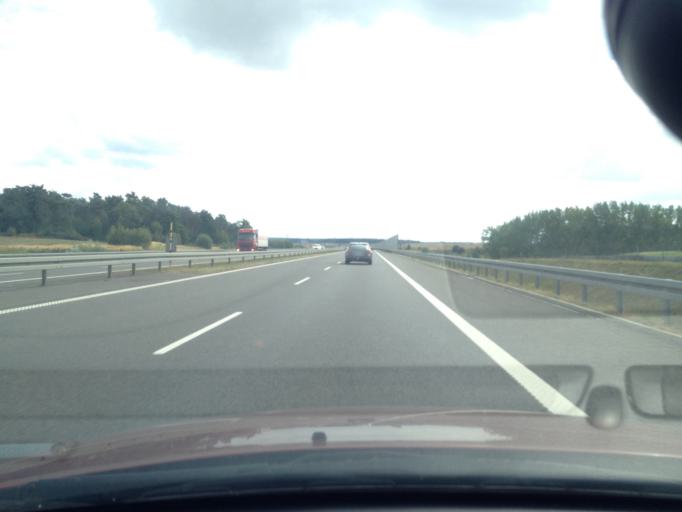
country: PL
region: West Pomeranian Voivodeship
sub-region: Powiat pyrzycki
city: Bielice
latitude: 53.2483
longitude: 14.6355
